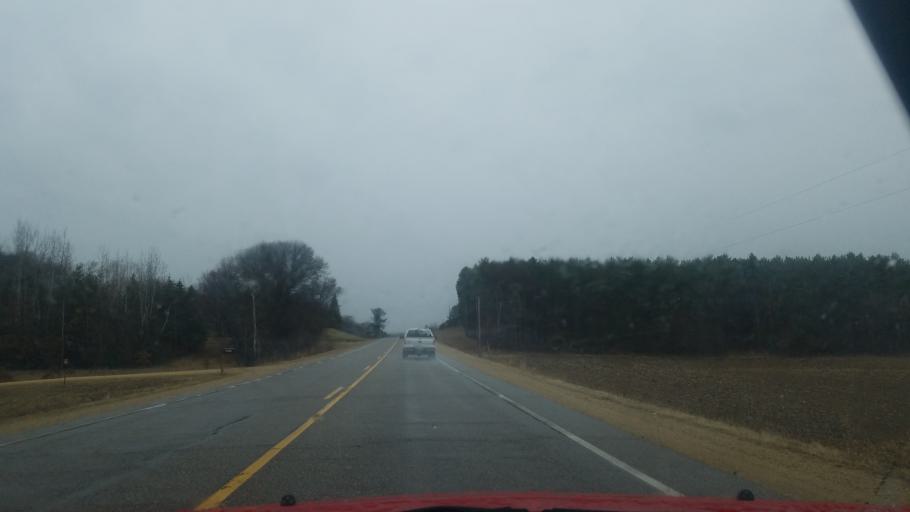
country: US
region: Wisconsin
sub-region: Dunn County
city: Tainter Lake
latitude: 45.0242
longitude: -91.8906
